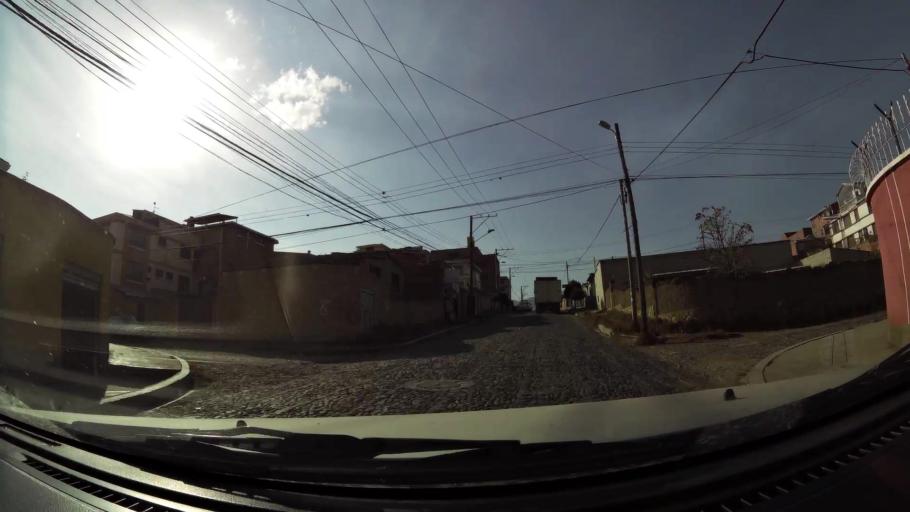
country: BO
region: La Paz
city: La Paz
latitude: -16.5198
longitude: -68.0835
